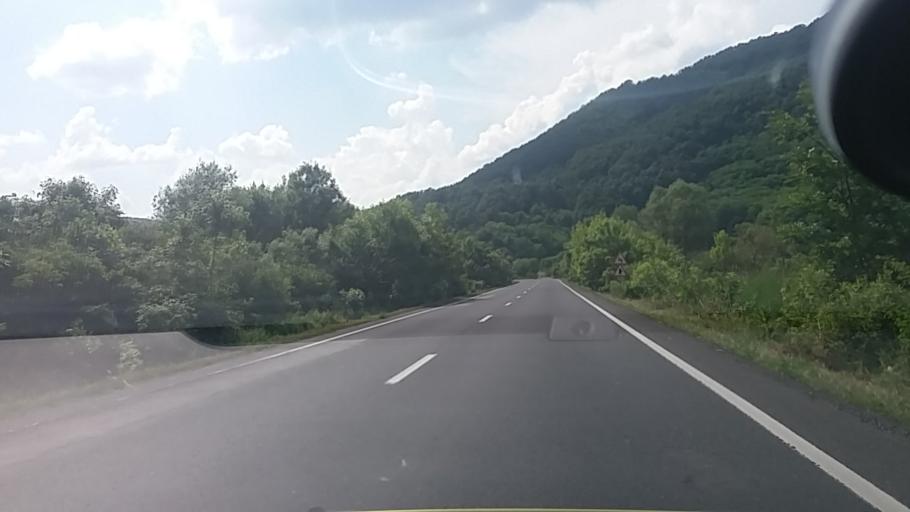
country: RO
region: Hunedoara
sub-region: Comuna Zam
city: Zam
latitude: 45.9727
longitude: 22.4551
